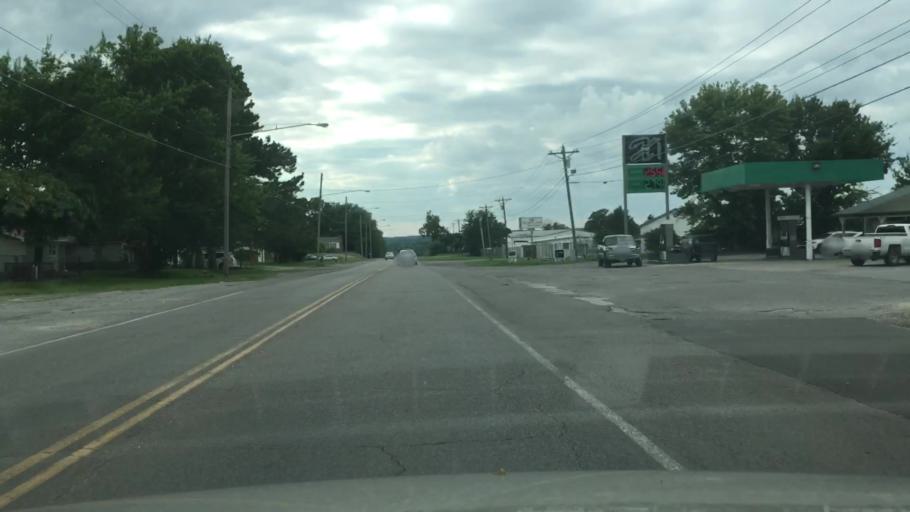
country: US
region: Oklahoma
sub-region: Cherokee County
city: Tahlequah
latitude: 35.9171
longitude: -94.9908
